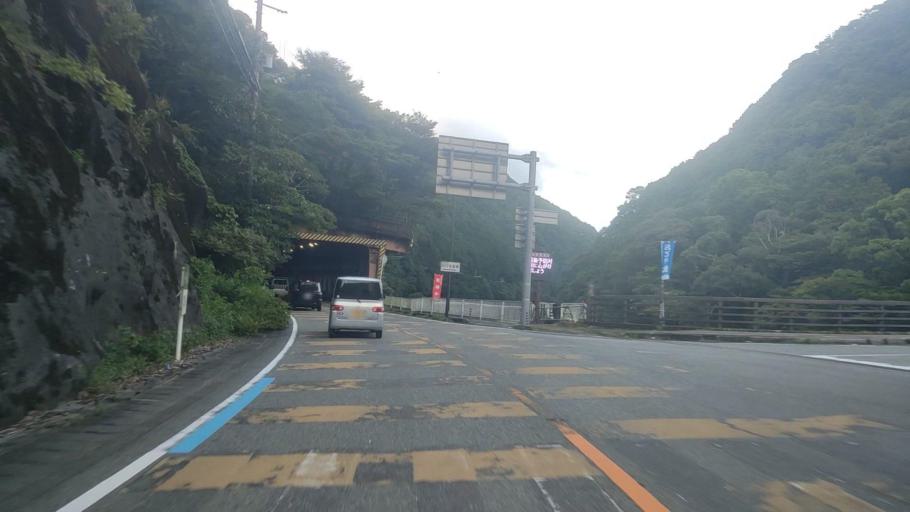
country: JP
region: Wakayama
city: Tanabe
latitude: 33.7756
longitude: 135.5030
